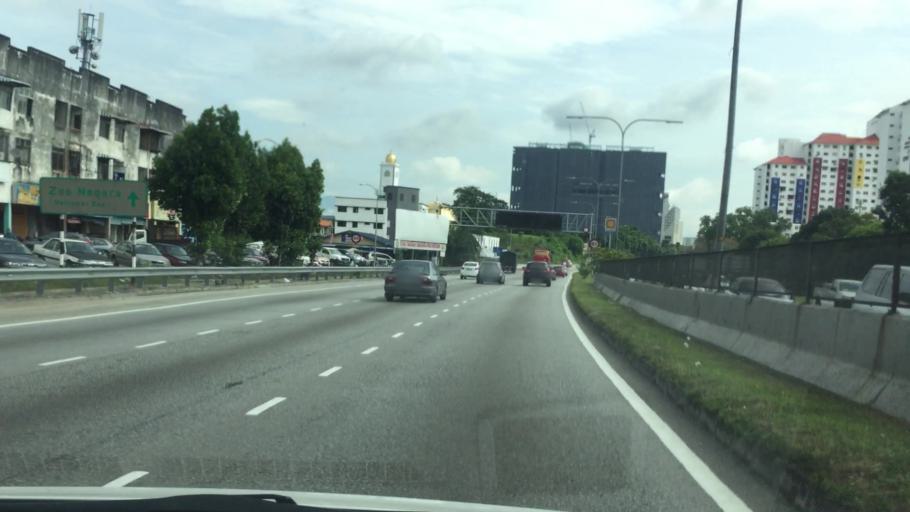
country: MY
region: Kuala Lumpur
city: Kuala Lumpur
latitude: 3.1484
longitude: 101.7445
